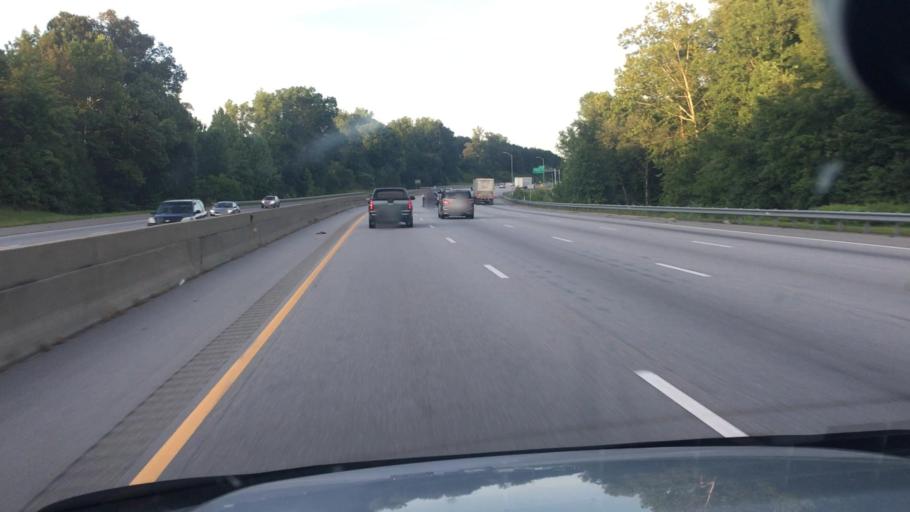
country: US
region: North Carolina
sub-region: Gaston County
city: Bessemer City
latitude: 35.2583
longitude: -81.2880
